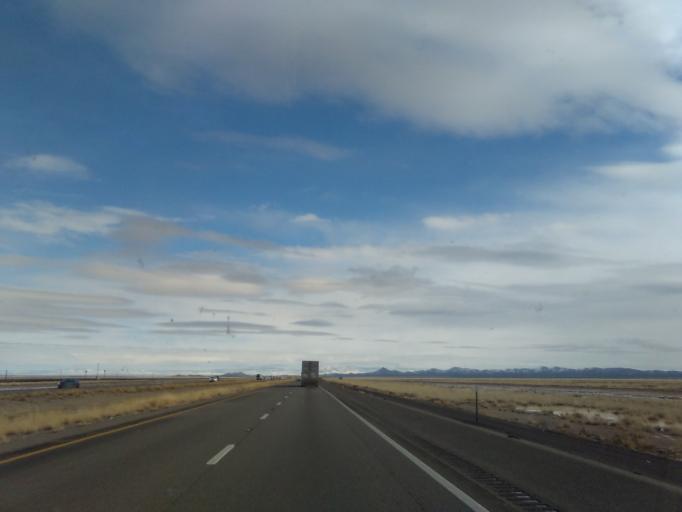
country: US
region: New Mexico
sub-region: Hidalgo County
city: Lordsburg
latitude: 32.2556
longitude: -108.9225
